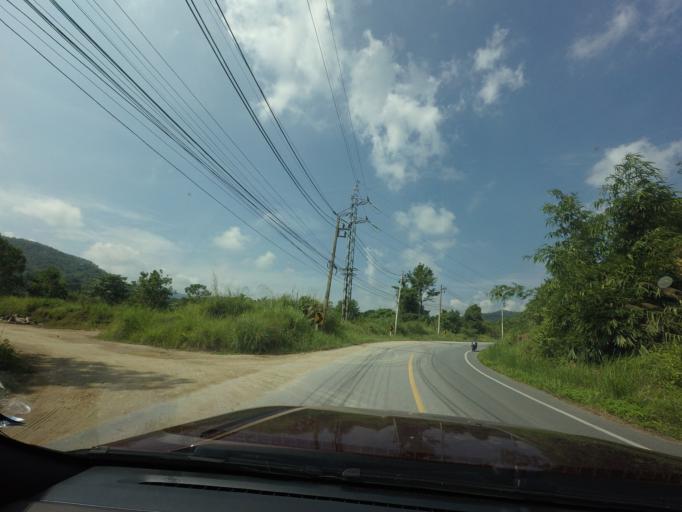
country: TH
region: Yala
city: Betong
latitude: 5.9256
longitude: 101.1813
